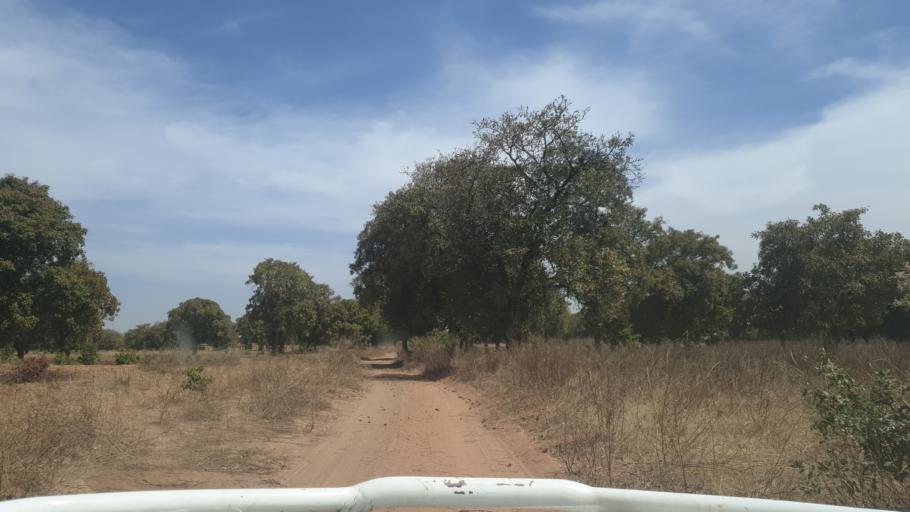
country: ML
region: Sikasso
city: Yorosso
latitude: 12.2896
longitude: -4.6699
